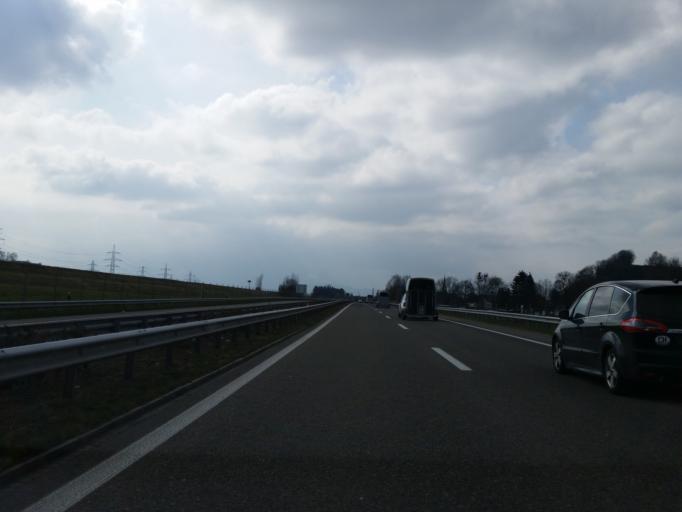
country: AT
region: Vorarlberg
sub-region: Politischer Bezirk Feldkirch
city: Koblach
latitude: 47.3443
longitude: 9.5959
